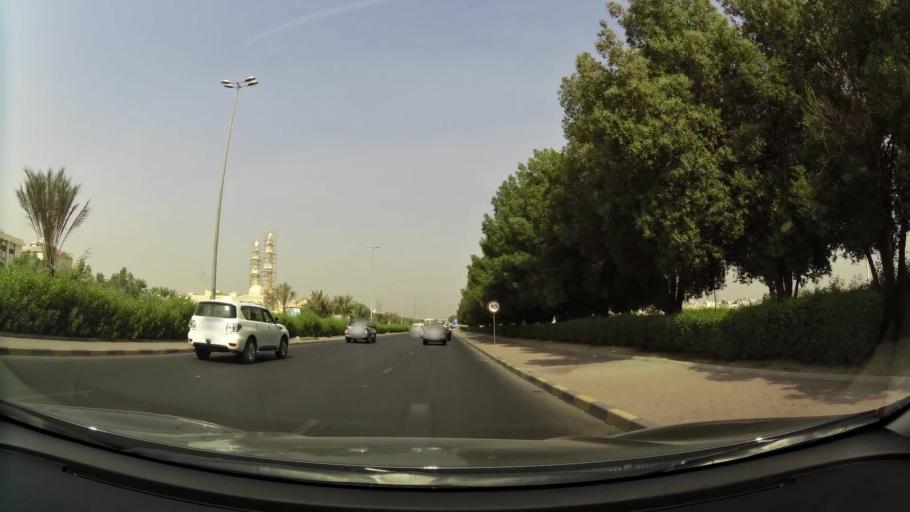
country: KW
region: Al Asimah
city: Ar Rabiyah
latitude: 29.2898
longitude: 47.9062
